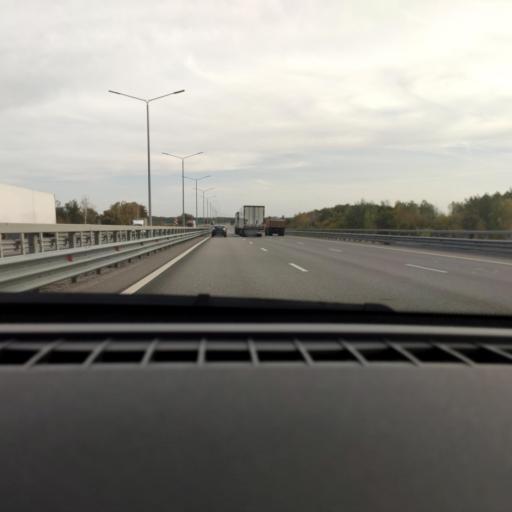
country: RU
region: Voronezj
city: Somovo
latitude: 51.7919
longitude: 39.2708
